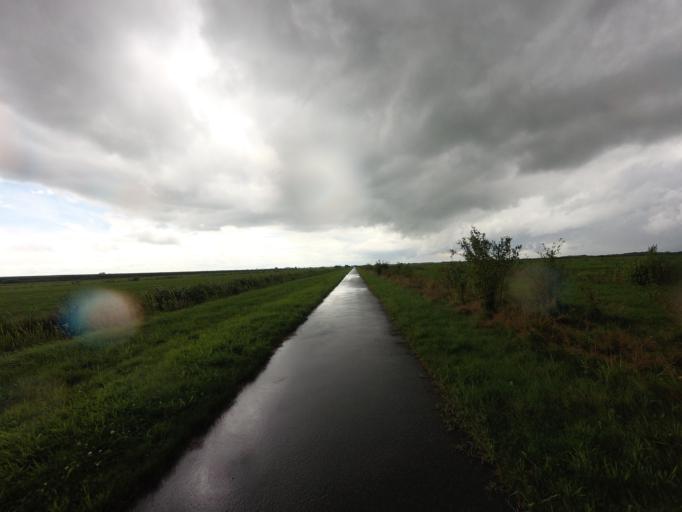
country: NL
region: North Holland
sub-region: Gemeente Wijdemeren
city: Nieuw-Loosdrecht
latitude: 52.1784
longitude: 5.1540
